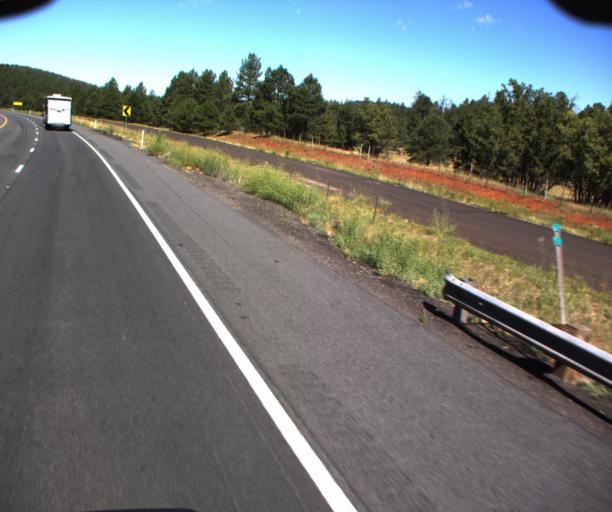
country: US
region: Arizona
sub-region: Coconino County
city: Williams
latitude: 35.2217
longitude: -112.2920
